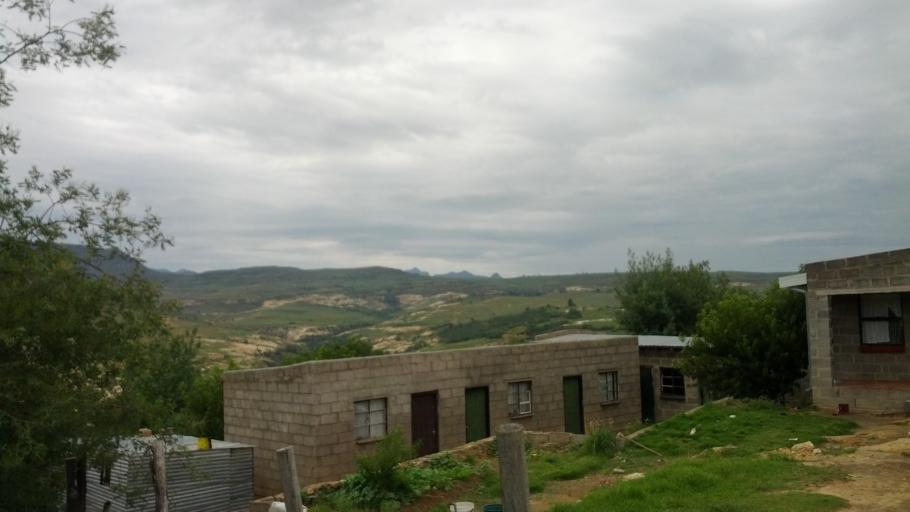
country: LS
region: Berea
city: Teyateyaneng
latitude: -29.1192
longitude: 27.9648
